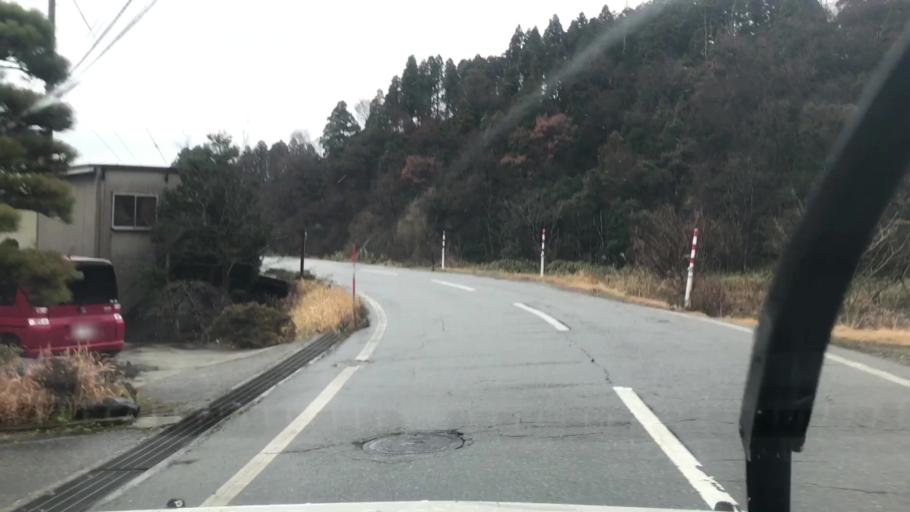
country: JP
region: Toyama
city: Kamiichi
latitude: 36.6050
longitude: 137.2924
